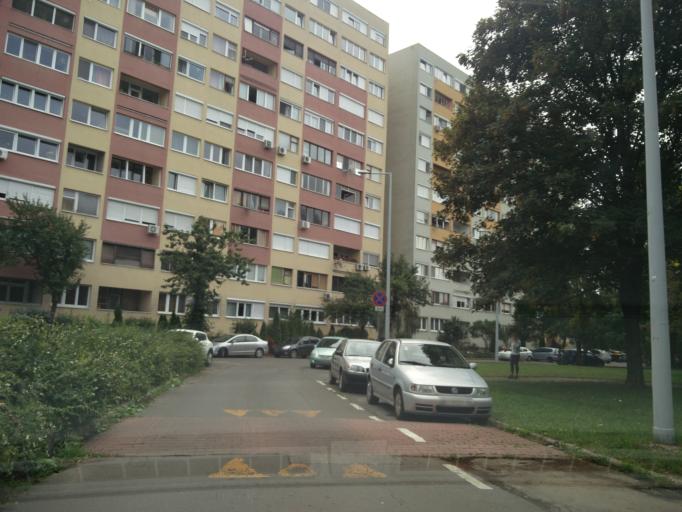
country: HU
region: Budapest
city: Budapest XI. keruelet
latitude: 47.4604
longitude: 19.0164
